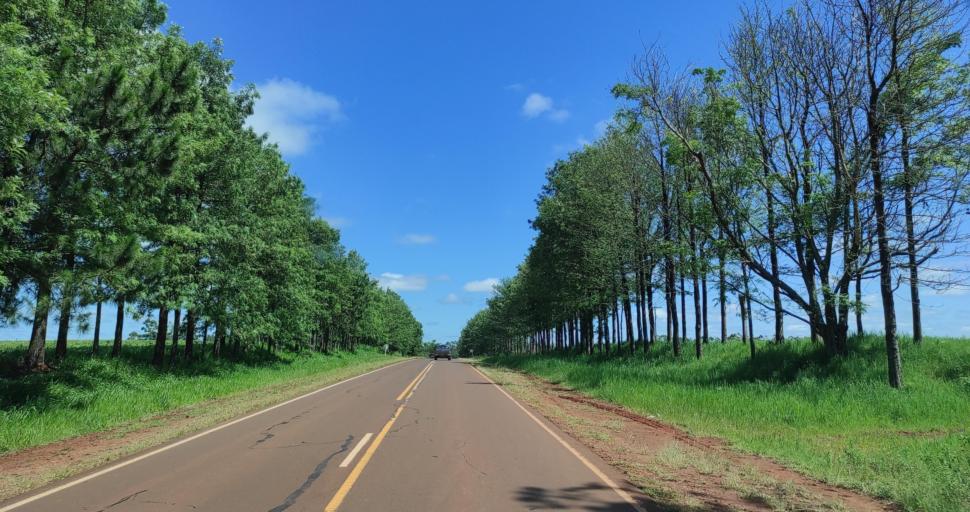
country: AR
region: Misiones
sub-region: Departamento de Veinticinco de Mayo
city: Veinticinco de Mayo
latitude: -27.4083
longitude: -54.7467
